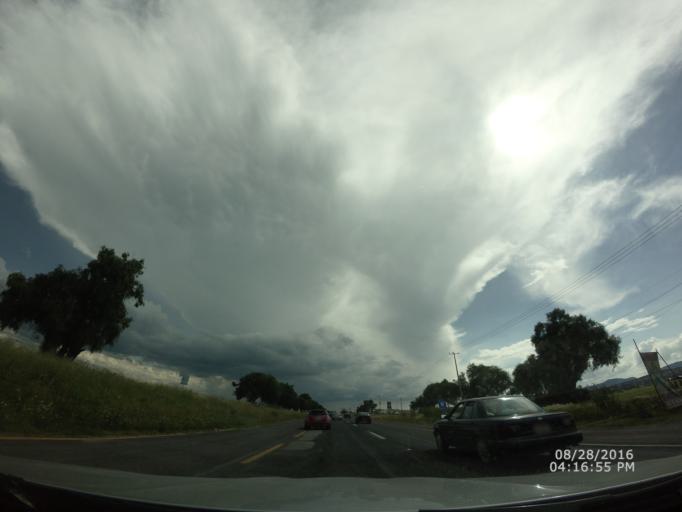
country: MX
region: Hidalgo
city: Zapotlan de Juarez
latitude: 19.9821
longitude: -98.8467
